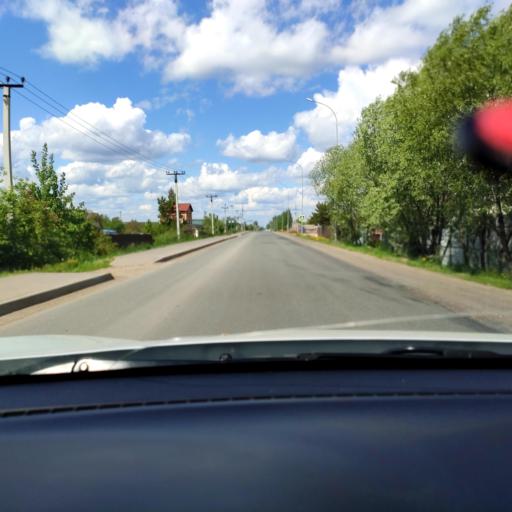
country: RU
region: Tatarstan
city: Stolbishchi
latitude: 55.6952
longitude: 49.1980
